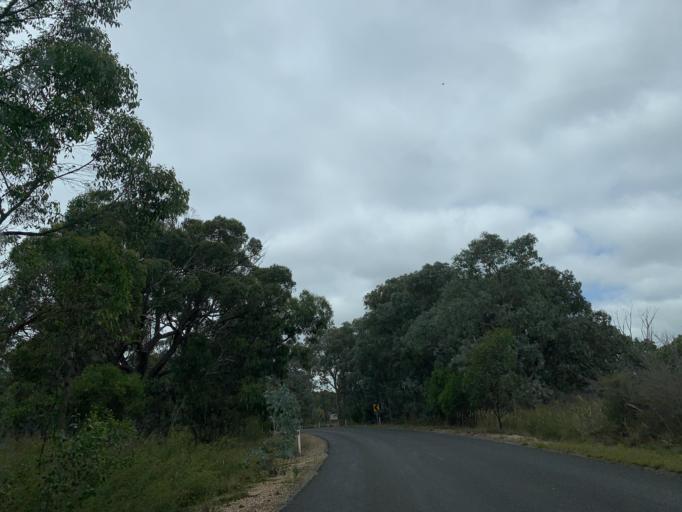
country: AU
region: Victoria
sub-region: Wellington
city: Heyfield
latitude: -37.9339
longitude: 146.7693
